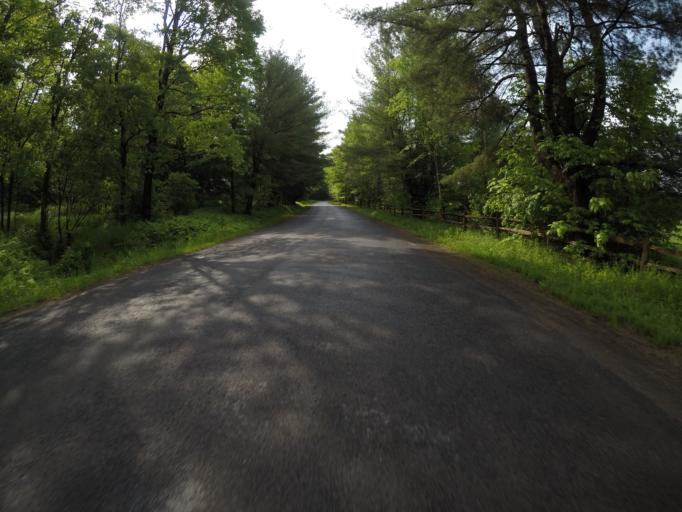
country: US
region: New York
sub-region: Delaware County
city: Stamford
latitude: 42.1801
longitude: -74.6706
